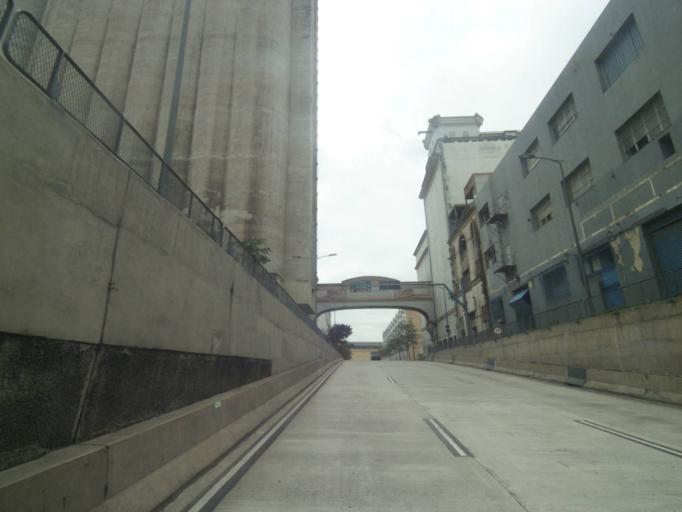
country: BR
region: Rio de Janeiro
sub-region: Rio De Janeiro
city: Rio de Janeiro
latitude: -22.8943
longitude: -43.1891
